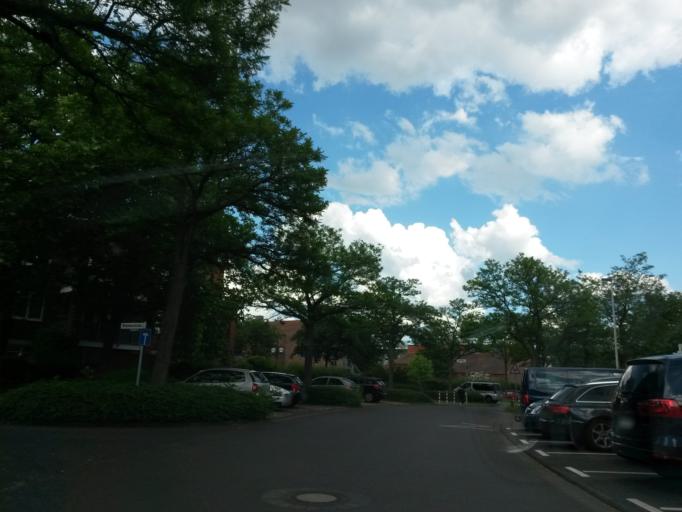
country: DE
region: North Rhine-Westphalia
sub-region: Regierungsbezirk Koln
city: Alfter
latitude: 50.6961
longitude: 7.0535
